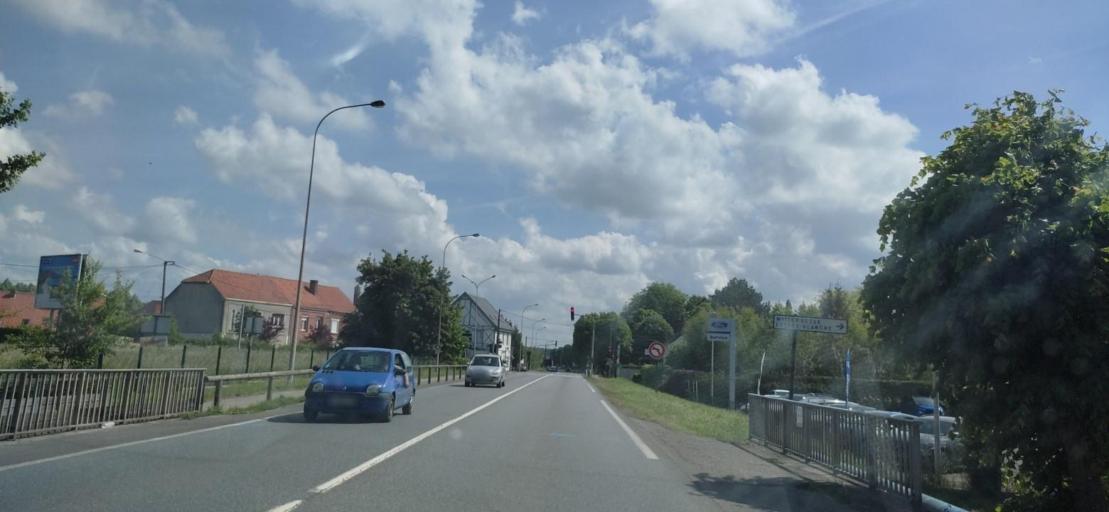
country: FR
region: Nord-Pas-de-Calais
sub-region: Departement du Pas-de-Calais
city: Aire-sur-la-Lys
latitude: 50.6337
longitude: 2.3894
